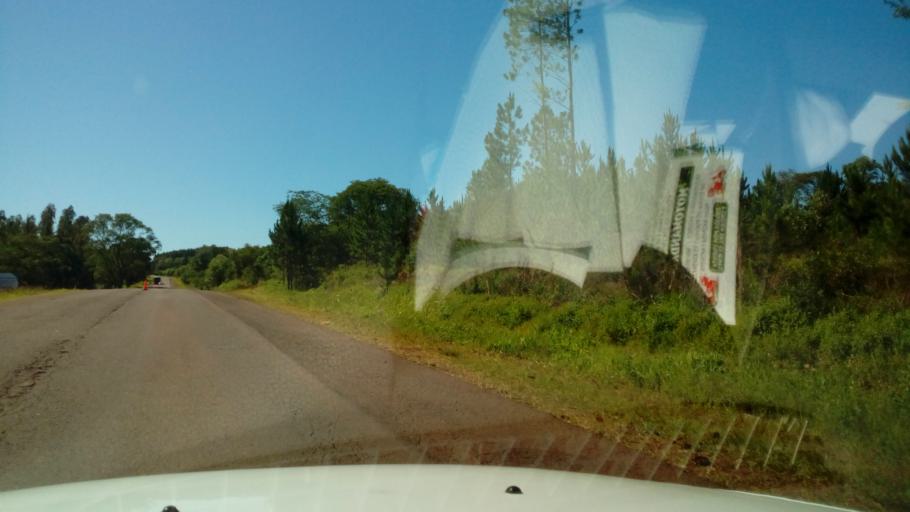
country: AR
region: Misiones
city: Almafuerte
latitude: -27.5532
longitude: -55.4228
